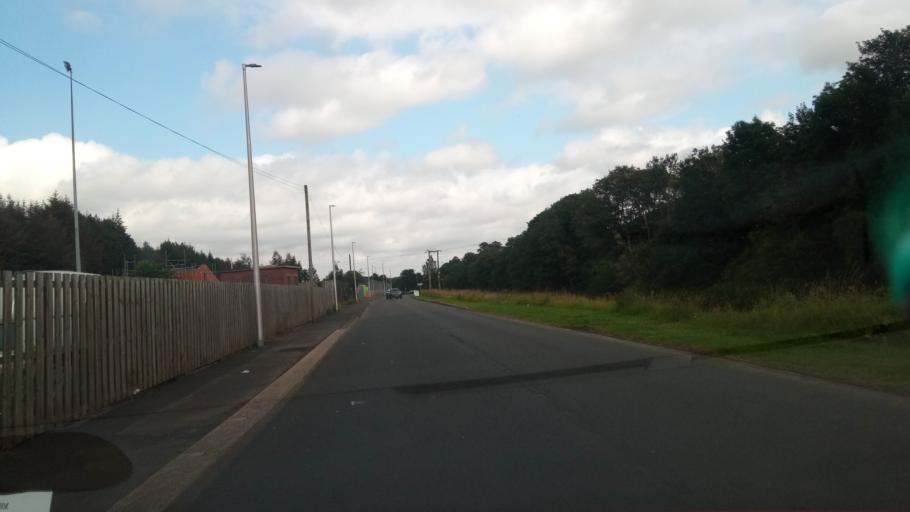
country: GB
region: Scotland
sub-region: The Scottish Borders
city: Hawick
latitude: 55.4326
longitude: -2.7621
